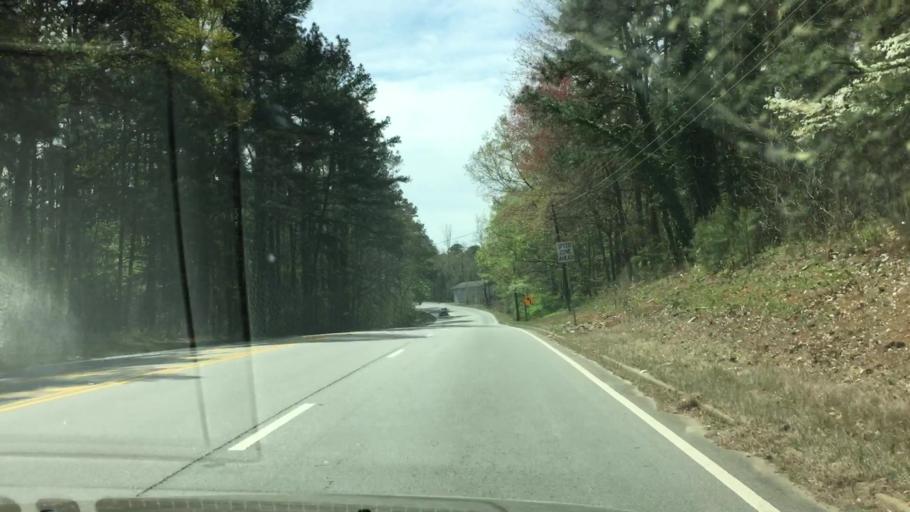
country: US
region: Georgia
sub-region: Barrow County
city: Winder
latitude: 34.0228
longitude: -83.7105
